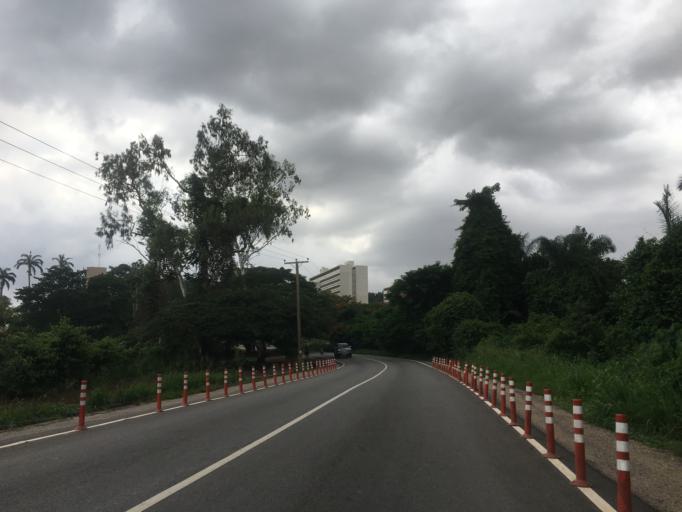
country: GH
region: Ashanti
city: Kumasi
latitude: 6.6783
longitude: -1.5691
